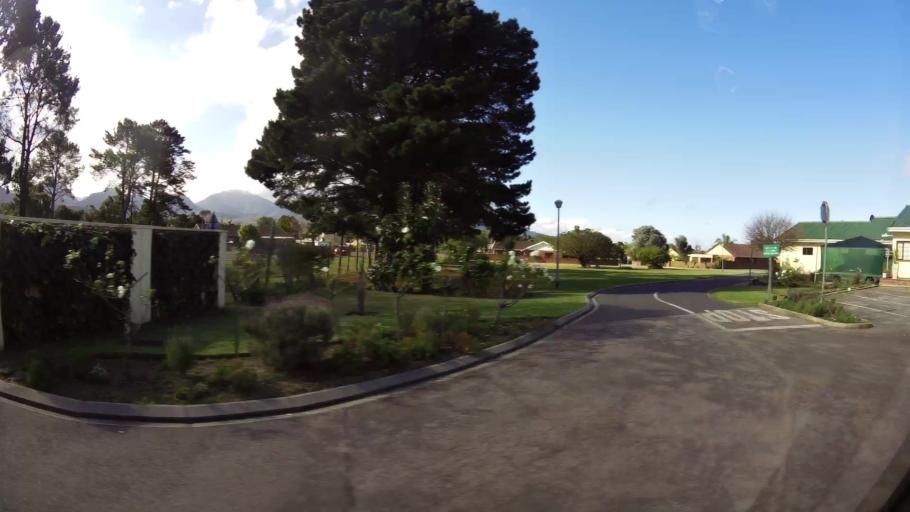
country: ZA
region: Western Cape
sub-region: Eden District Municipality
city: George
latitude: -33.9684
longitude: 22.4883
